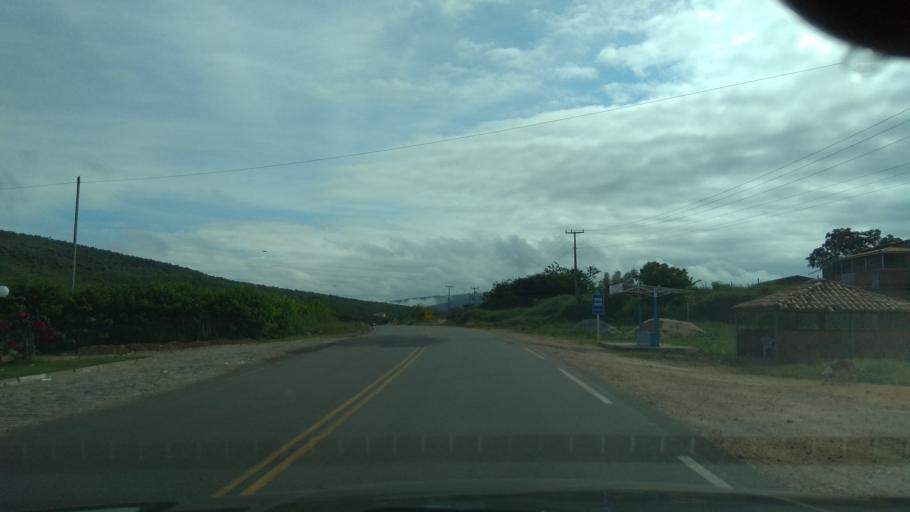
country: BR
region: Bahia
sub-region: Santa Ines
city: Santa Ines
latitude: -13.3473
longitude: -39.8739
